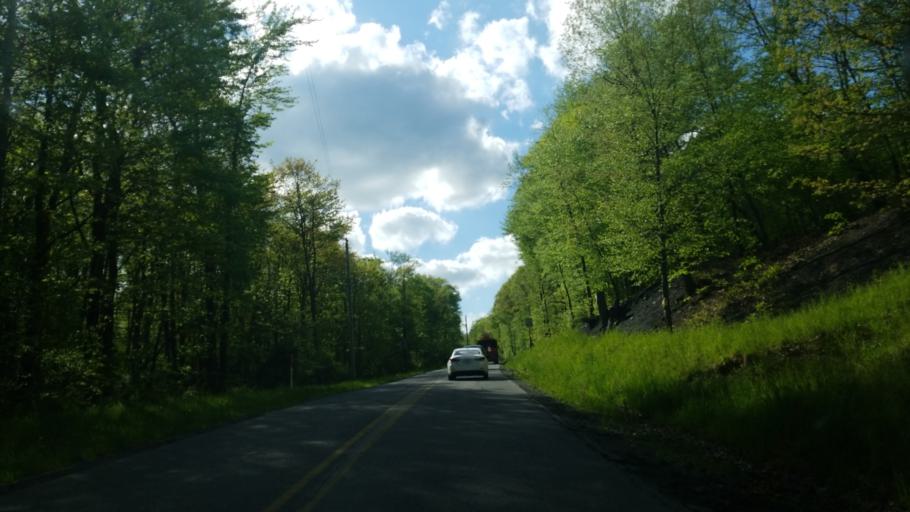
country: US
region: Pennsylvania
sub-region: Clearfield County
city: Osceola Mills
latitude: 40.9347
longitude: -78.3133
